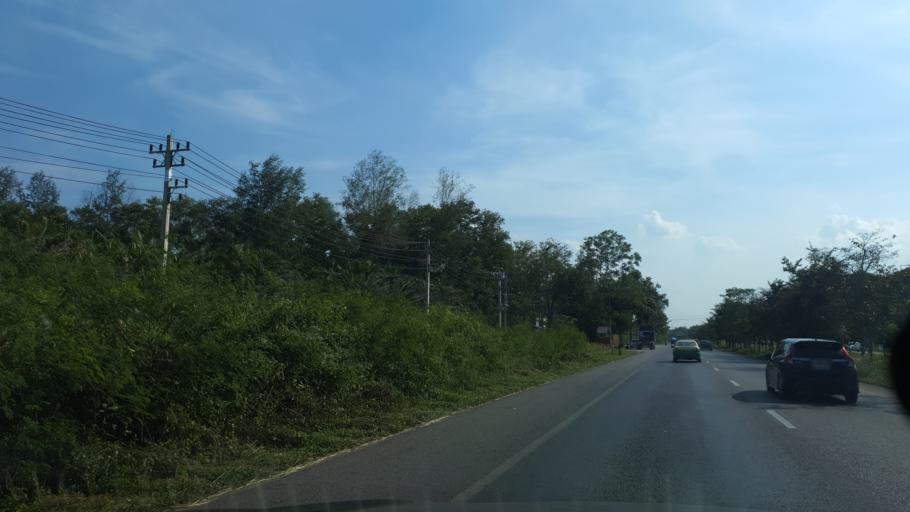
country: TH
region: Surat Thani
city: Phunphin
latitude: 9.0409
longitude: 99.1726
